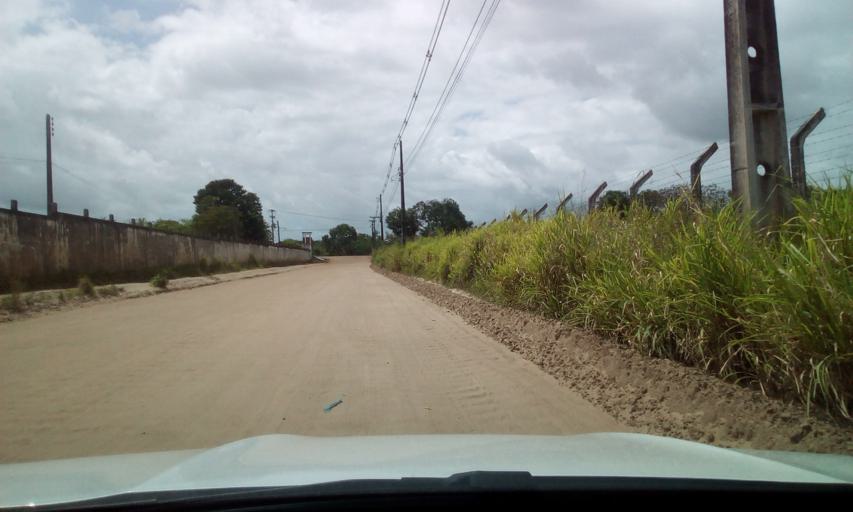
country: BR
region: Paraiba
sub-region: Bayeux
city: Bayeux
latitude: -7.1395
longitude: -34.9491
